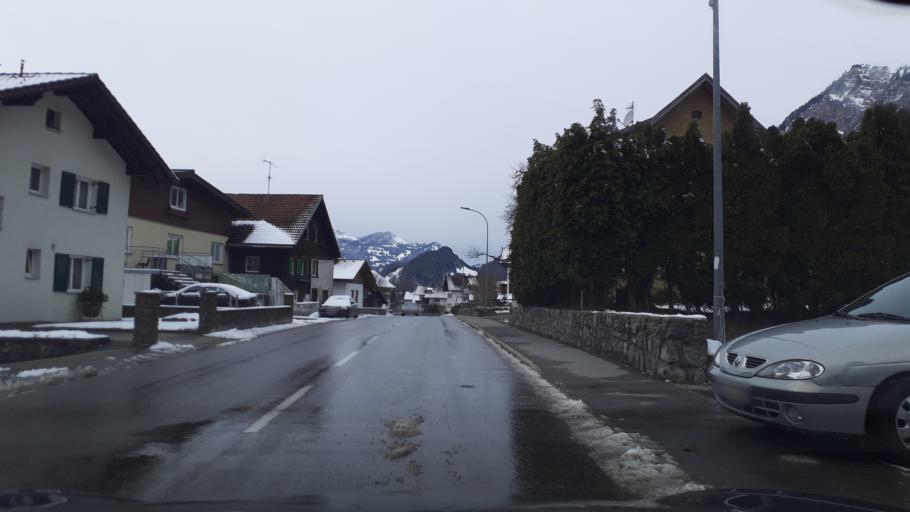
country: AT
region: Vorarlberg
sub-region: Politischer Bezirk Bludenz
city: Innerbraz
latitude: 47.1455
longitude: 9.9108
